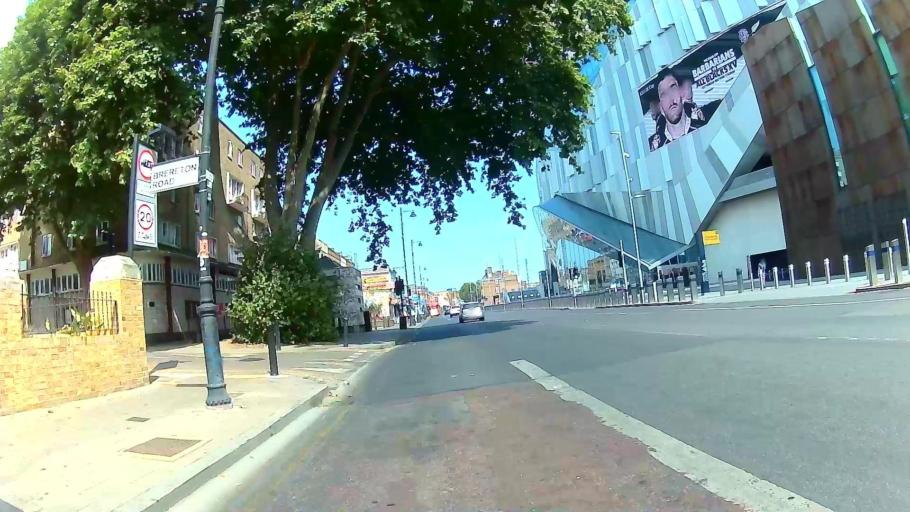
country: GB
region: England
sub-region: Greater London
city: Harringay
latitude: 51.6033
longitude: -0.0679
